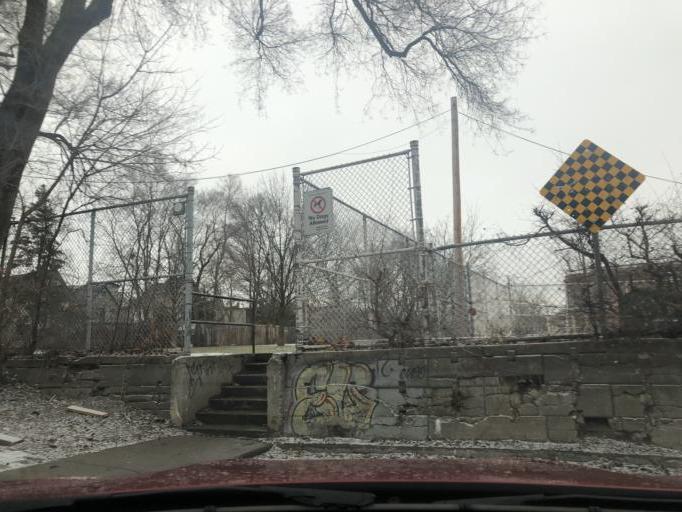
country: CA
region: Ontario
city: Toronto
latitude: 43.6770
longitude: -79.3417
